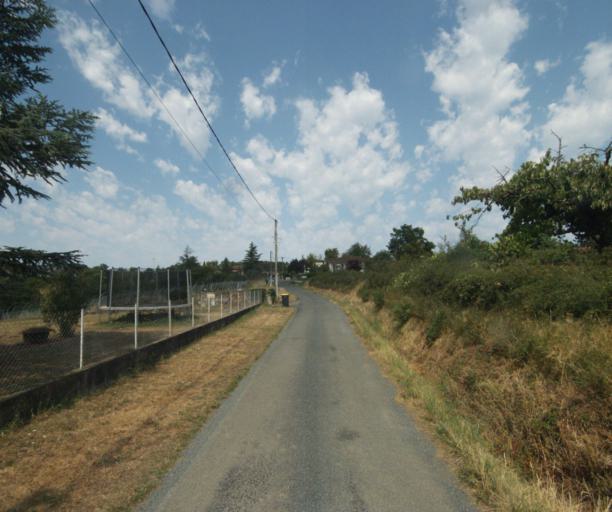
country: FR
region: Rhone-Alpes
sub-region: Departement du Rhone
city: Lentilly
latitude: 45.8333
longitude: 4.6583
